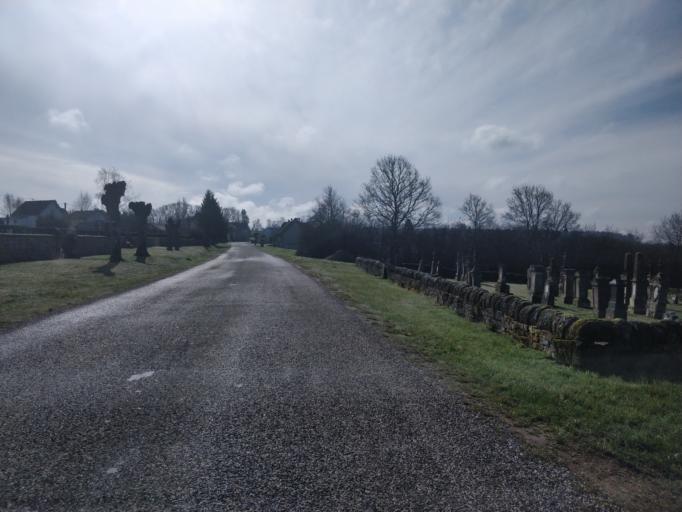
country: FR
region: Alsace
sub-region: Departement du Bas-Rhin
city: Drulingen
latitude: 48.8975
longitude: 7.2523
